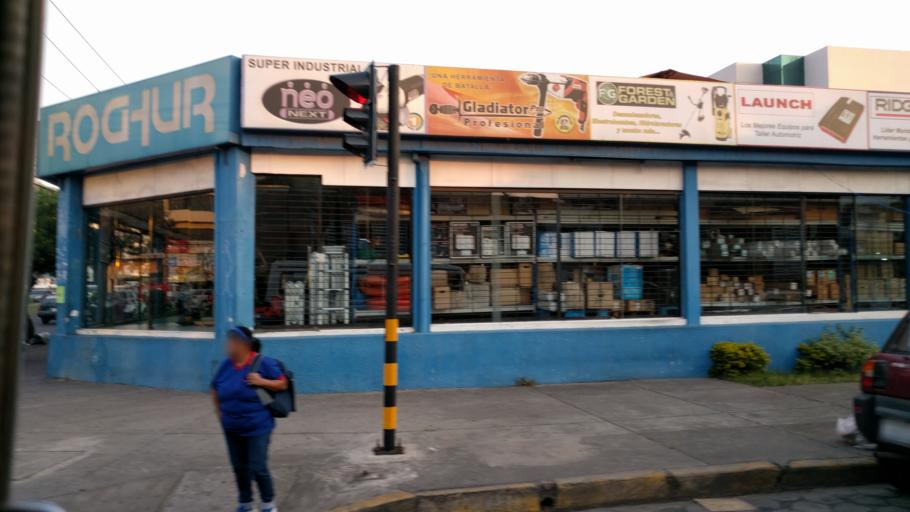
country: BO
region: Santa Cruz
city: Santa Cruz de la Sierra
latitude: -17.7812
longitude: -63.1890
